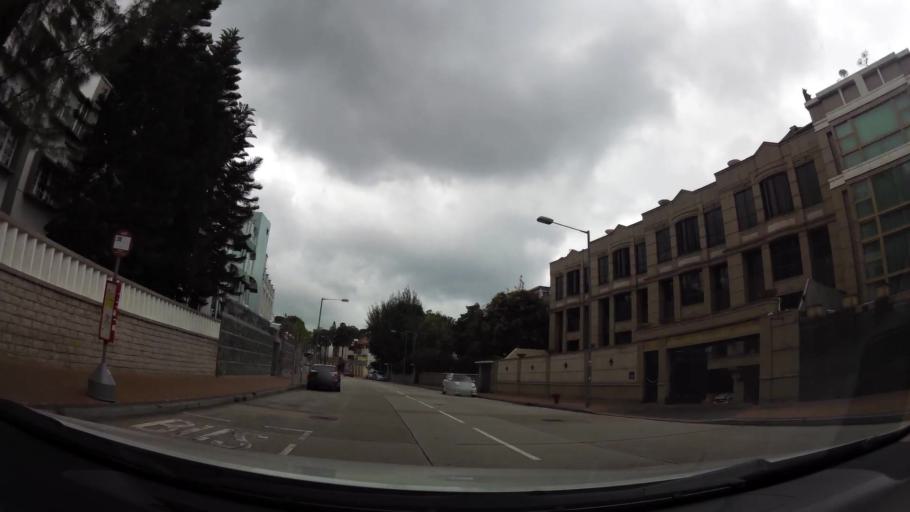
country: HK
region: Wong Tai Sin
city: Wong Tai Sin
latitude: 22.3334
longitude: 114.1818
